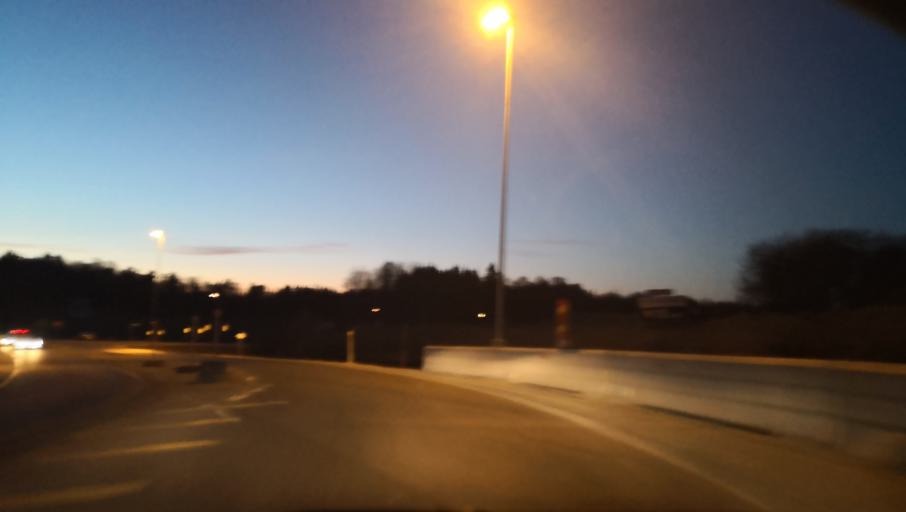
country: SE
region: Stockholm
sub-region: Nynashamns Kommun
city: Nynashamn
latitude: 58.9279
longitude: 17.9343
